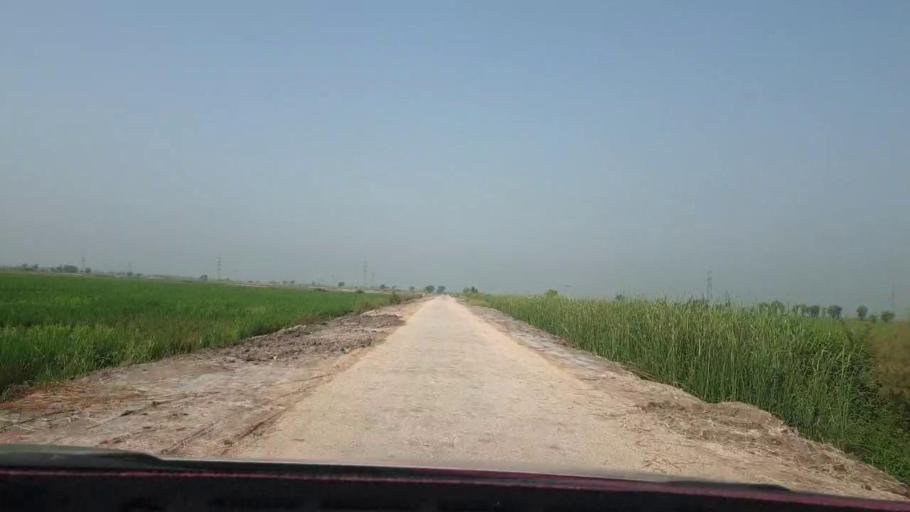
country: PK
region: Sindh
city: Nasirabad
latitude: 27.4310
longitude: 67.9497
